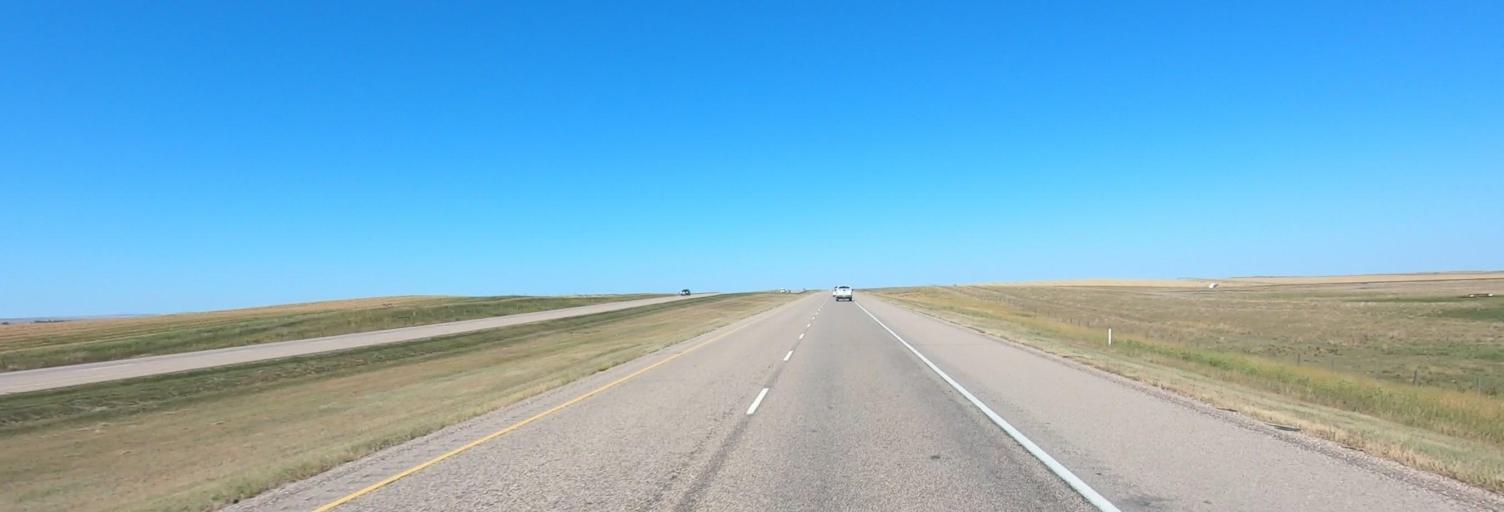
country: CA
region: Alberta
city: Bassano
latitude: 50.7221
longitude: -112.2786
